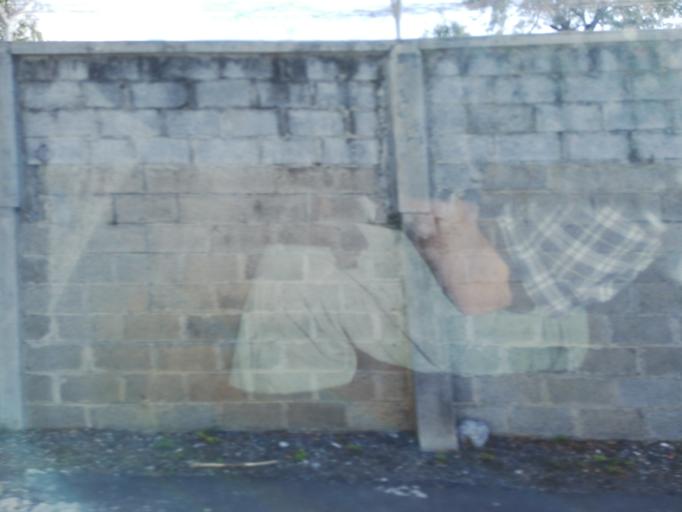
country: MU
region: Port Louis
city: Port Louis
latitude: -20.1643
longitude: 57.4869
